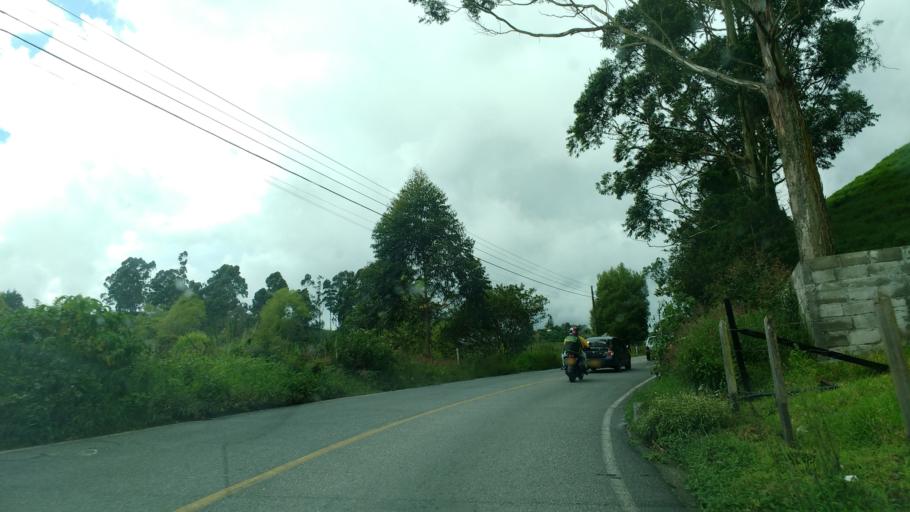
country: CO
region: Antioquia
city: Marinilla
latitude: 6.1981
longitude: -75.2847
